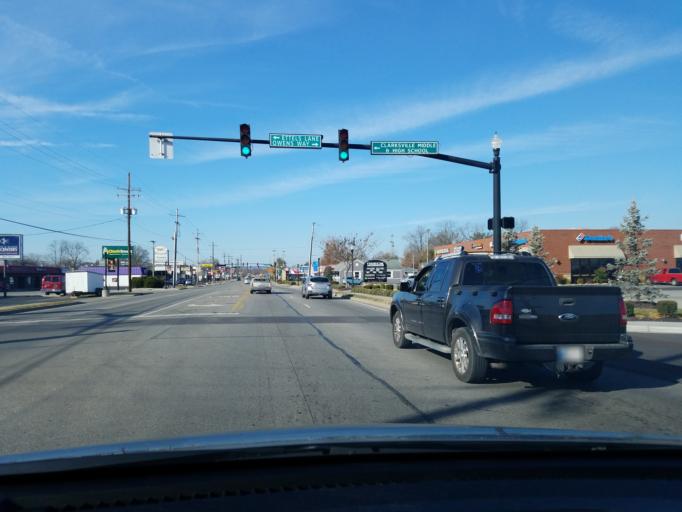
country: US
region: Indiana
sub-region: Clark County
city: Clarksville
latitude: 38.3028
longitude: -85.7644
